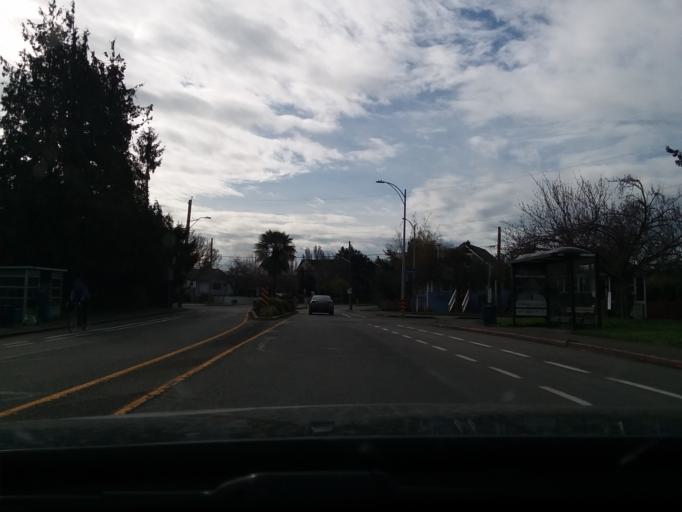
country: CA
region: British Columbia
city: Oak Bay
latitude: 48.4329
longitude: -123.3336
